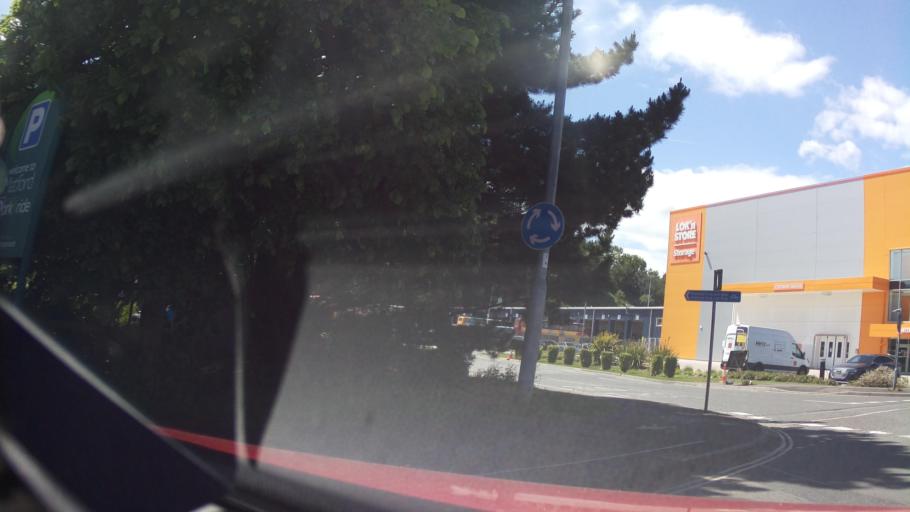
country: GB
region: England
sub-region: Devon
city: Exminster
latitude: 50.6952
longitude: -3.5194
